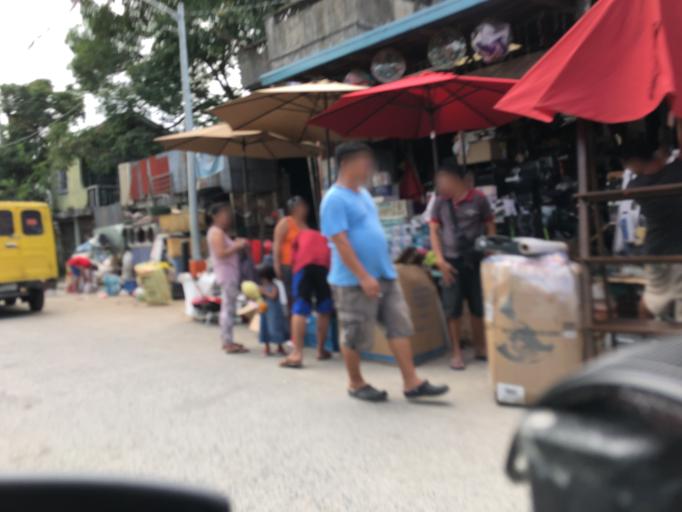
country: PH
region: Central Luzon
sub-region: Province of Bulacan
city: San Jose del Monte
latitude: 14.7513
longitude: 121.0572
